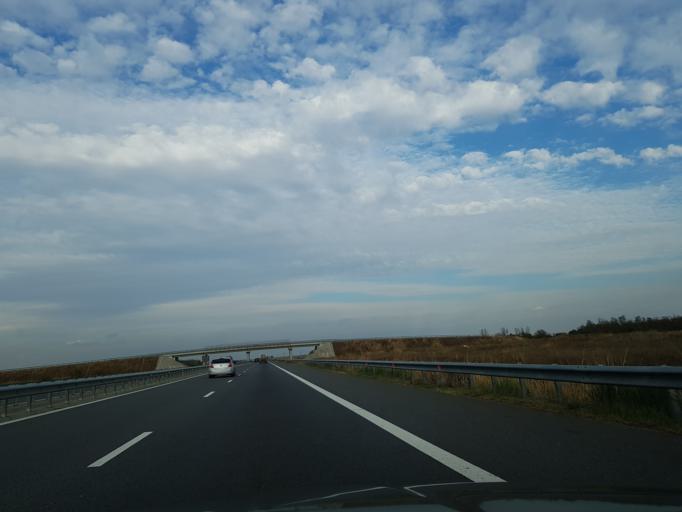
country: RO
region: Ilfov
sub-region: Comuna Gruiu
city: Gruiu
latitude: 44.7156
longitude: 26.2406
